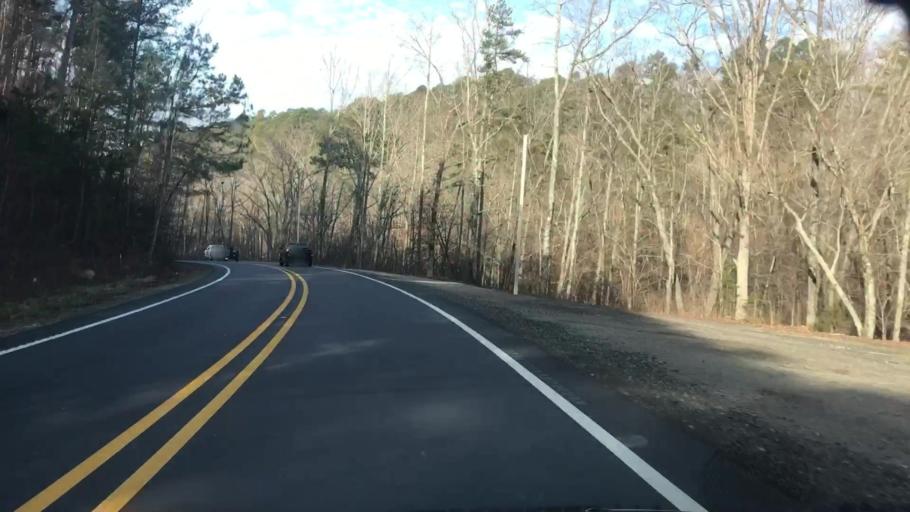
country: US
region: Arkansas
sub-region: Montgomery County
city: Mount Ida
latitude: 34.5244
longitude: -93.4019
